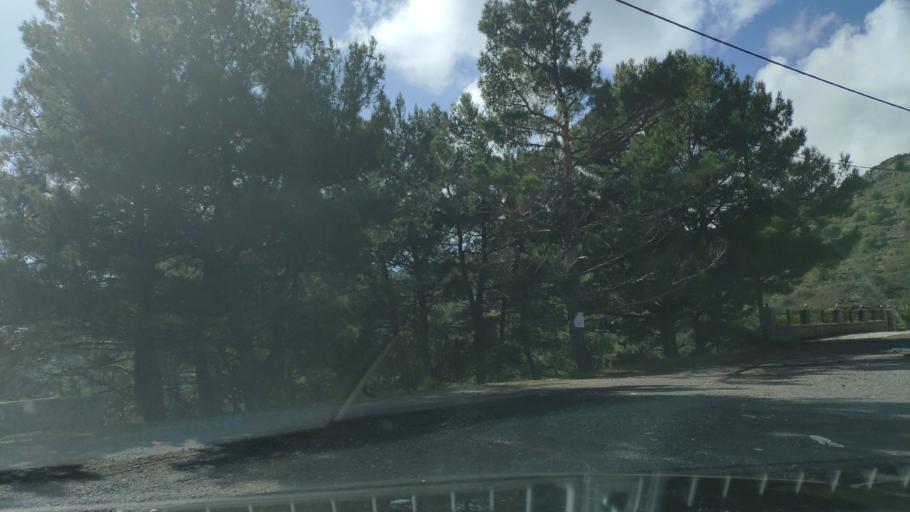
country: GR
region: Peloponnese
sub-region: Nomos Arkadias
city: Dimitsana
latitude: 37.5918
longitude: 22.0313
